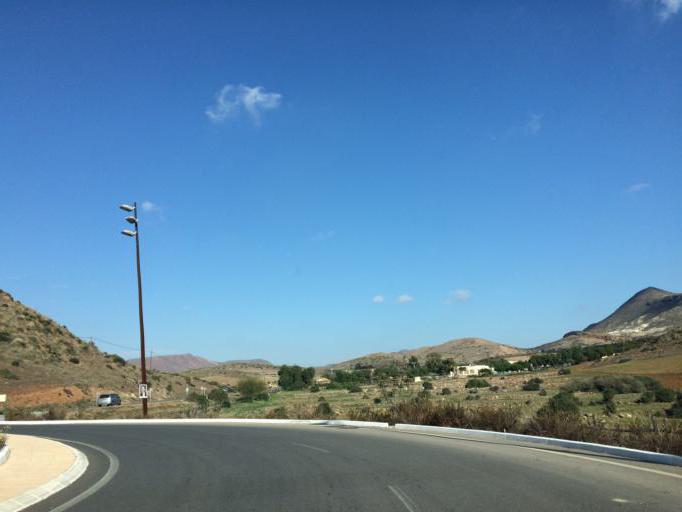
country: ES
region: Andalusia
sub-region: Provincia de Almeria
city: San Jose
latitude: 36.7687
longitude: -2.1089
